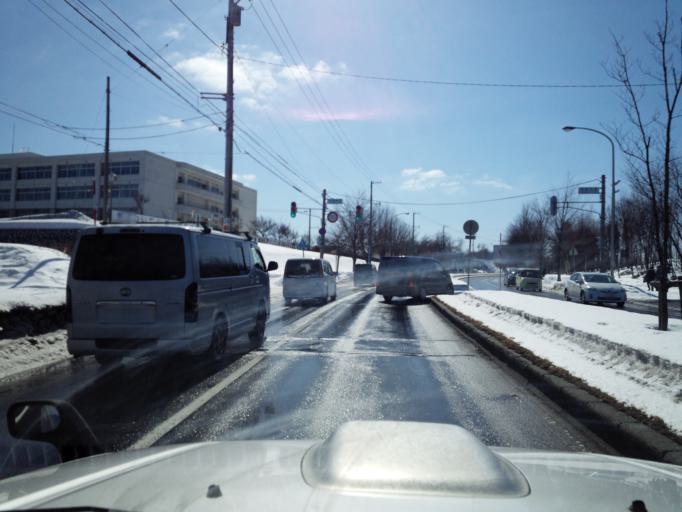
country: JP
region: Hokkaido
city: Kitahiroshima
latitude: 42.9984
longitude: 141.4610
